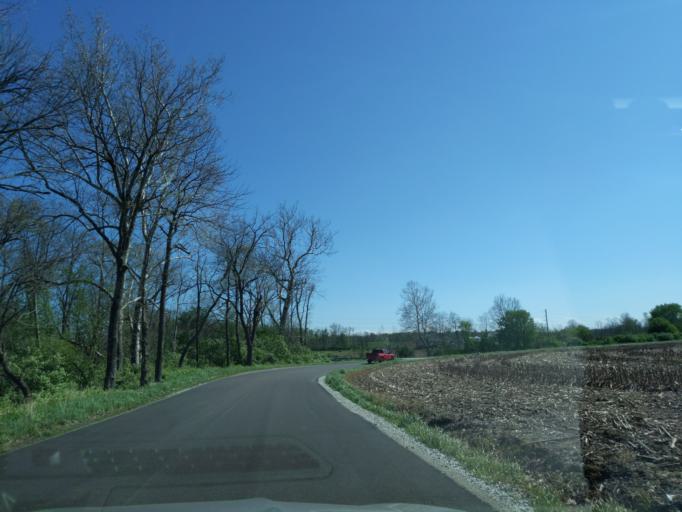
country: US
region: Indiana
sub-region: Decatur County
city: Greensburg
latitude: 39.2939
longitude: -85.4895
